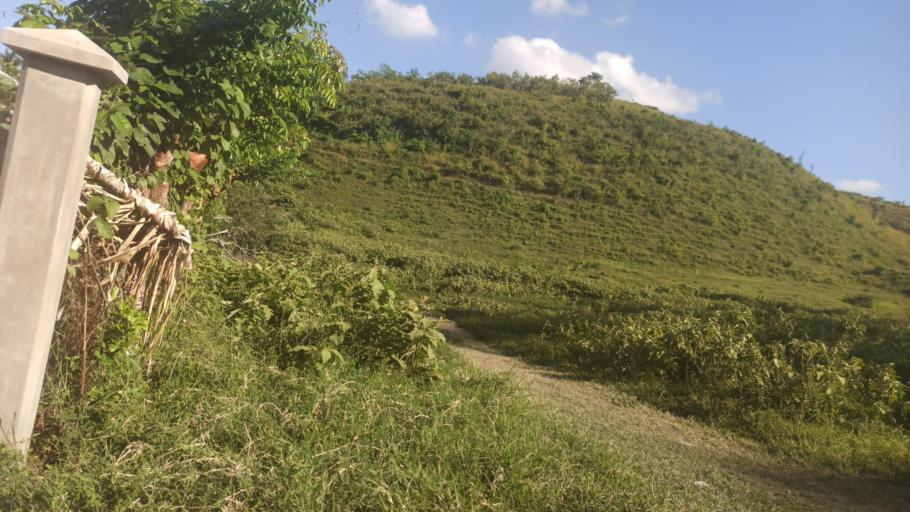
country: MX
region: Veracruz
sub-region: Poza Rica de Hidalgo
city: El Mollejon
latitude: 20.5559
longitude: -97.3974
